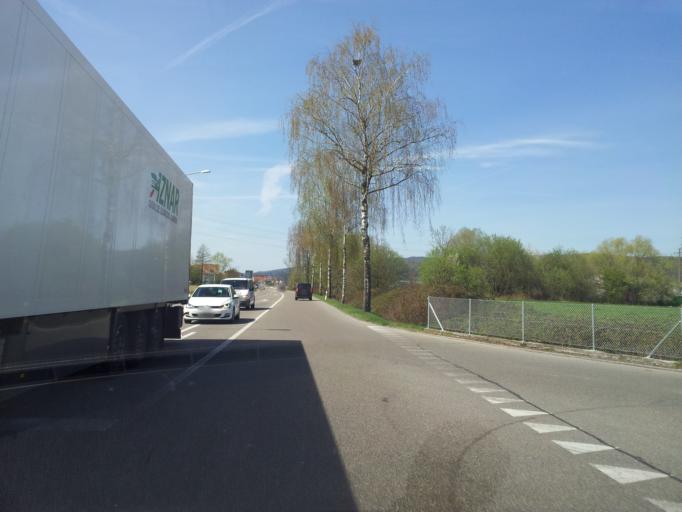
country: CH
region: Zurich
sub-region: Bezirk Dielsdorf
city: Regensdorf / Hofacher-Geeren
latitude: 47.4364
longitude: 8.4542
